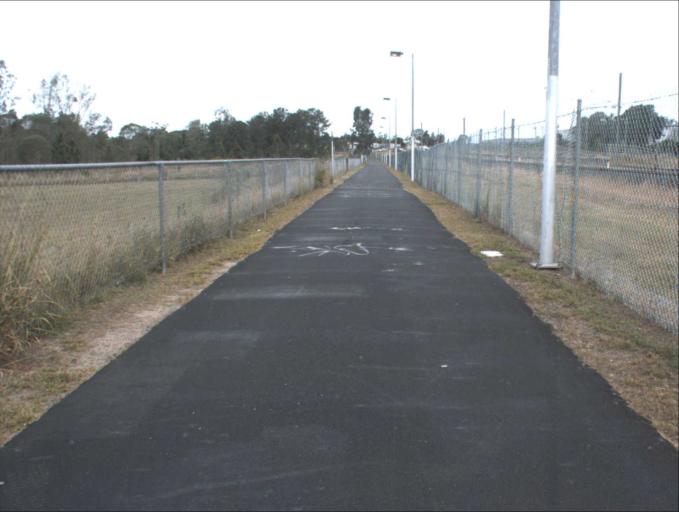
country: AU
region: Queensland
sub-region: Logan
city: Beenleigh
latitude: -27.7074
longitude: 153.1847
